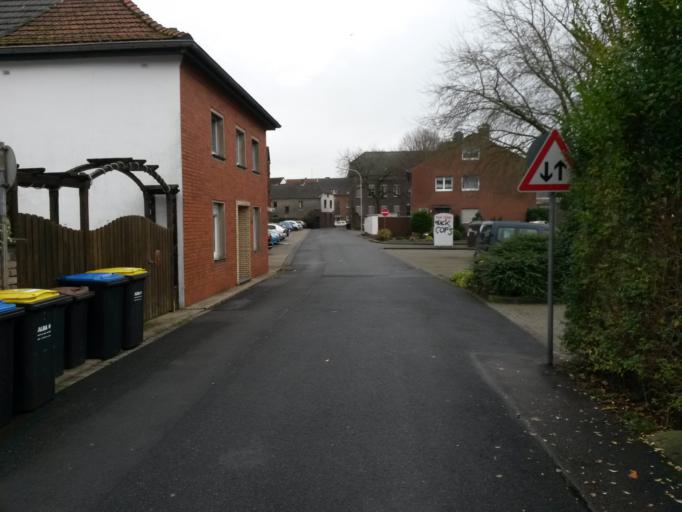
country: DE
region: North Rhine-Westphalia
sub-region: Regierungsbezirk Dusseldorf
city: Alpen
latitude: 51.5770
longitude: 6.5119
